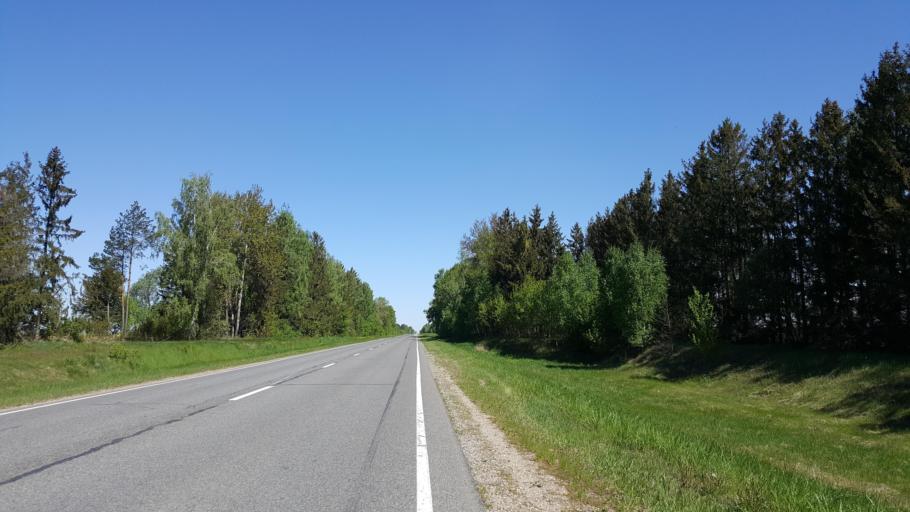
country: BY
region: Brest
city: Kamyanyets
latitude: 52.4246
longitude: 23.7870
